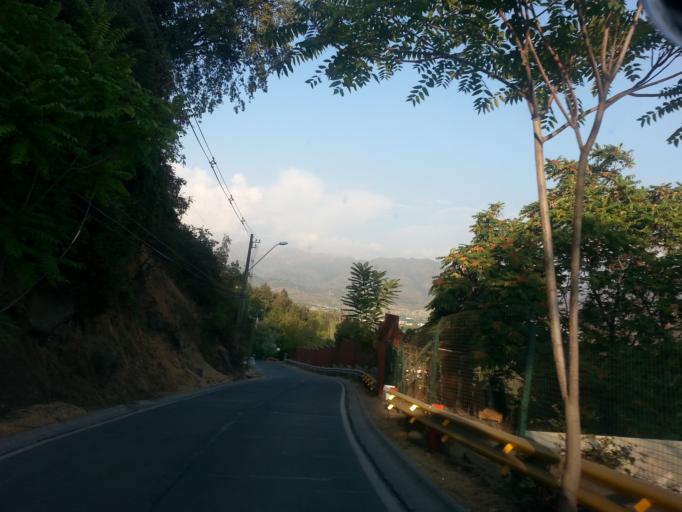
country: CL
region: Santiago Metropolitan
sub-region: Provincia de Santiago
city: Villa Presidente Frei, Nunoa, Santiago, Chile
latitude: -33.3641
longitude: -70.5576
